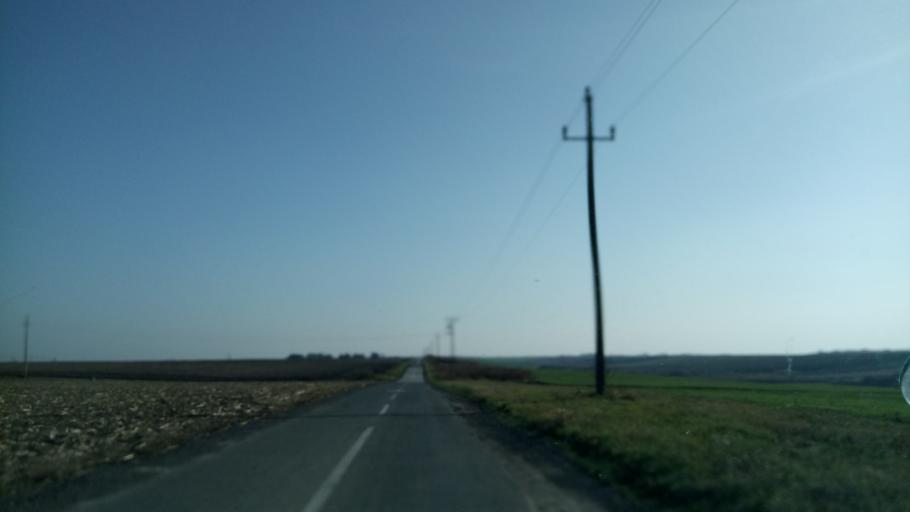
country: RS
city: Ljukovo
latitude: 45.0388
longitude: 20.0394
